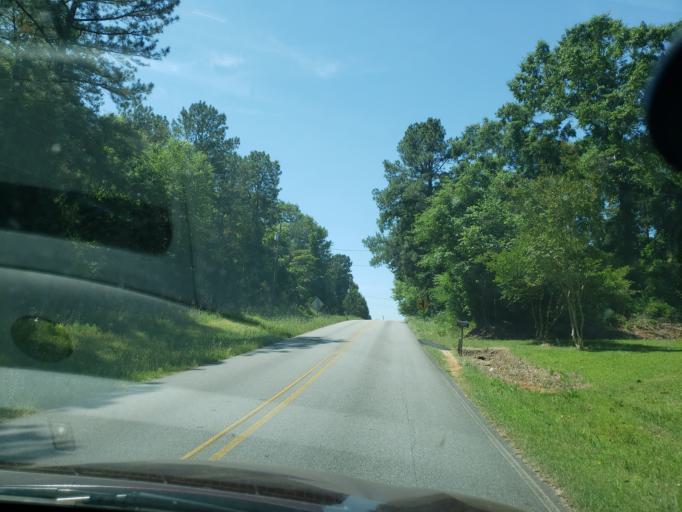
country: US
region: Alabama
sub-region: Elmore County
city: Tallassee
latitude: 32.5858
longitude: -85.8582
